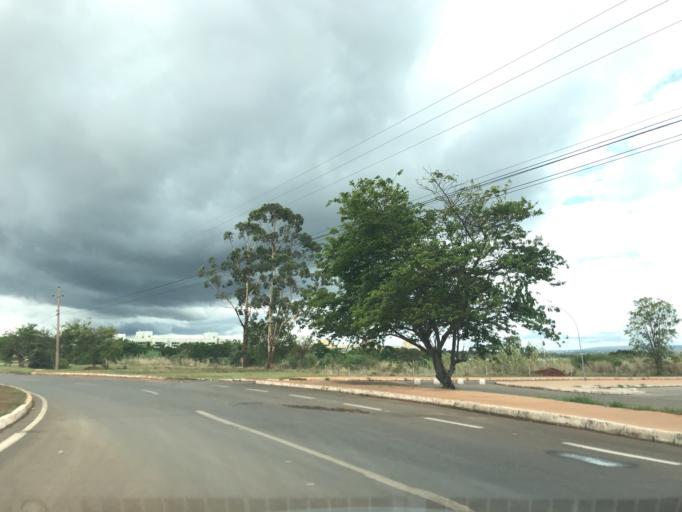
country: BR
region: Federal District
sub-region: Brasilia
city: Brasilia
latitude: -15.7901
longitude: -47.8374
